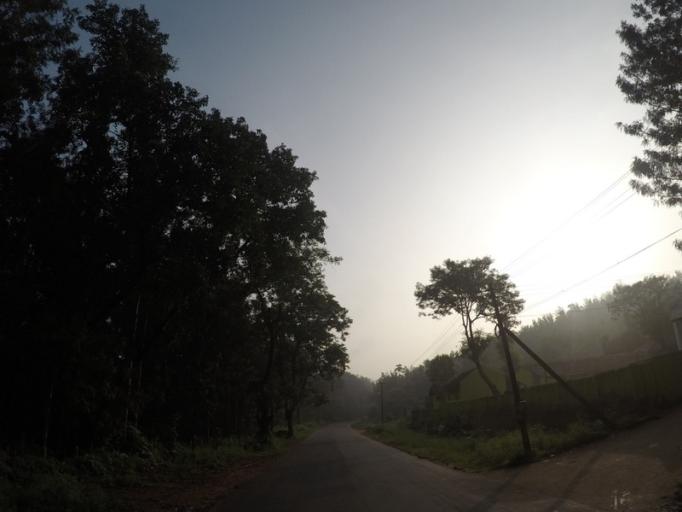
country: IN
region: Karnataka
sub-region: Chikmagalur
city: Chikmagalur
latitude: 13.3913
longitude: 75.7697
